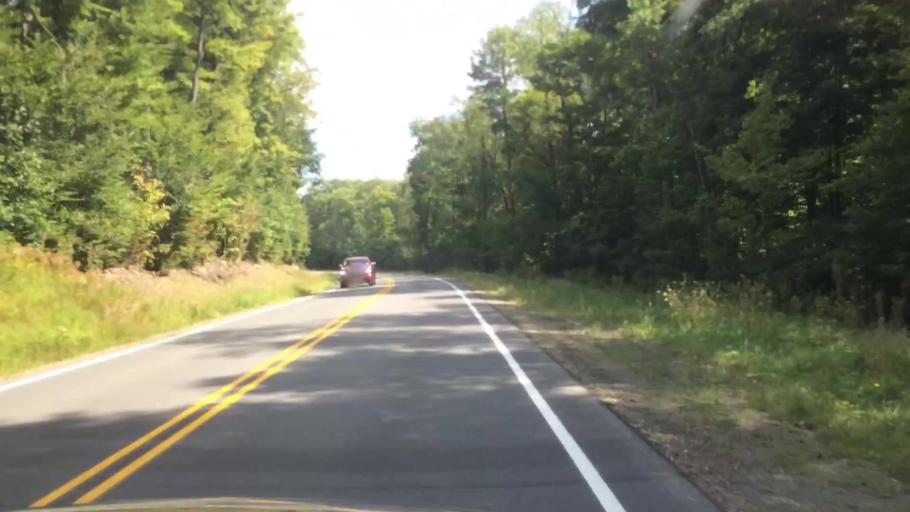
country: US
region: Pennsylvania
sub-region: McKean County
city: Bradford
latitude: 41.8868
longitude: -78.5946
